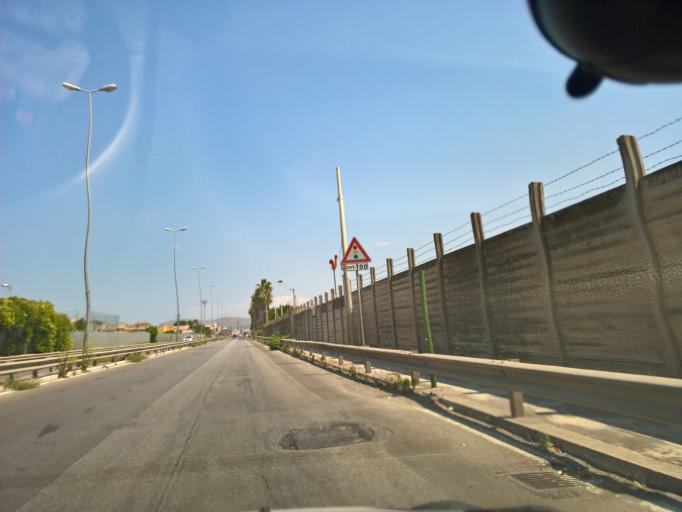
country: IT
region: Sicily
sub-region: Palermo
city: Ciaculli
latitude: 38.0929
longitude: 13.4061
